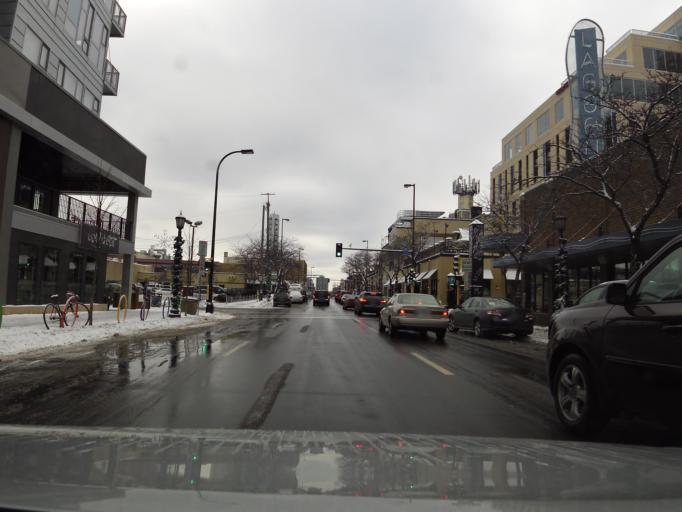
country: US
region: Minnesota
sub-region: Hennepin County
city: Minneapolis
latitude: 44.9493
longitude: -93.2965
